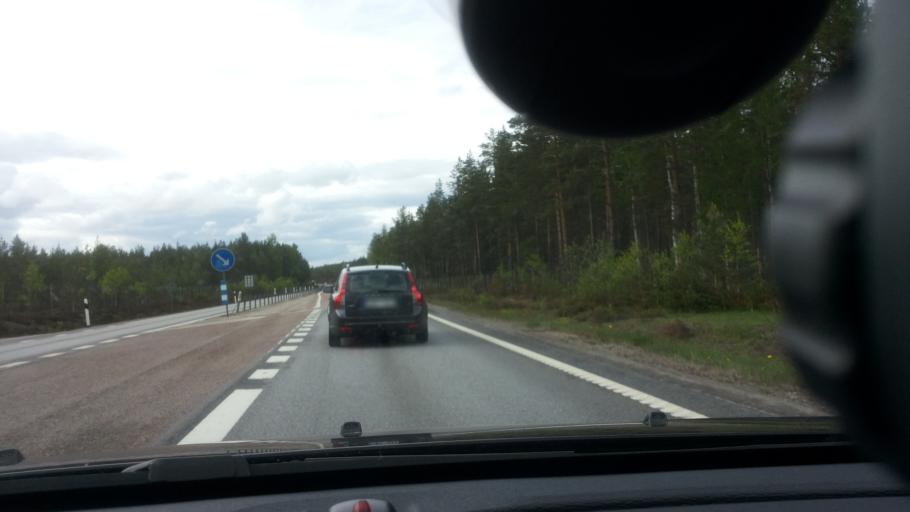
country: SE
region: Gaevleborg
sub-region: Gavle Kommun
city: Norrsundet
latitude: 60.9827
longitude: 17.0153
